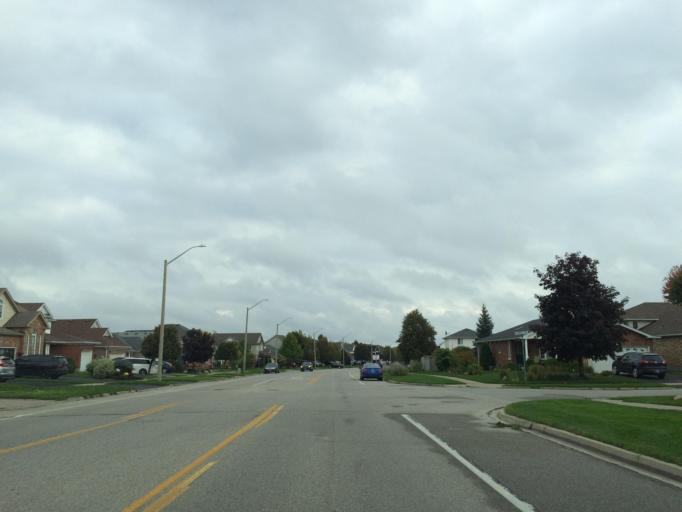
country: CA
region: Ontario
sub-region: Wellington County
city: Guelph
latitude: 43.5689
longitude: -80.2315
